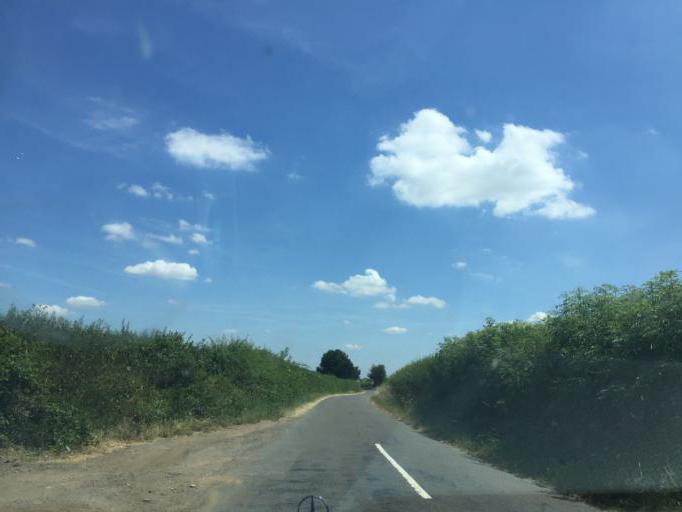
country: GB
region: England
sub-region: Leicestershire
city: Hinckley
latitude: 52.4900
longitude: -1.3475
